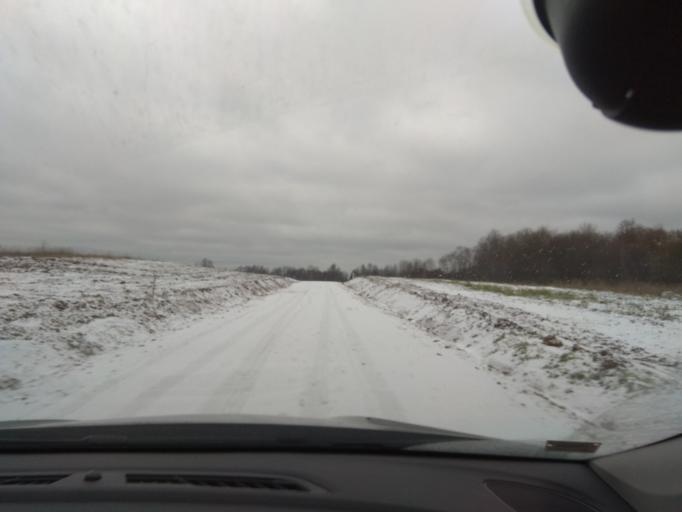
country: LT
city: Lentvaris
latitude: 54.6491
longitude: 25.0830
